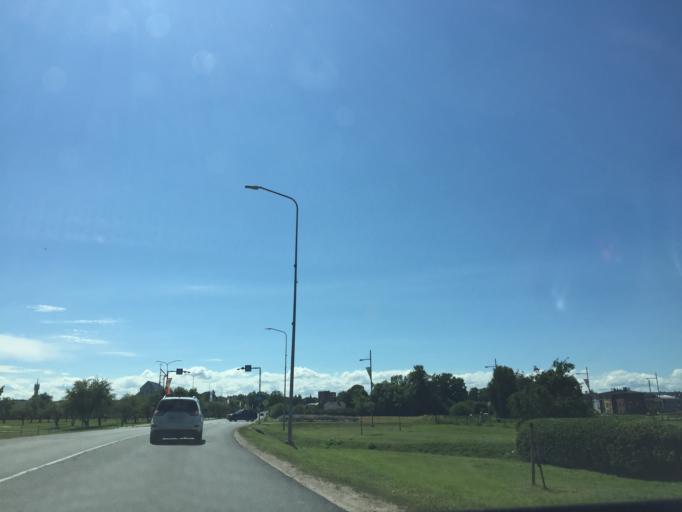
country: LV
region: Salaspils
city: Salaspils
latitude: 56.8584
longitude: 24.3473
